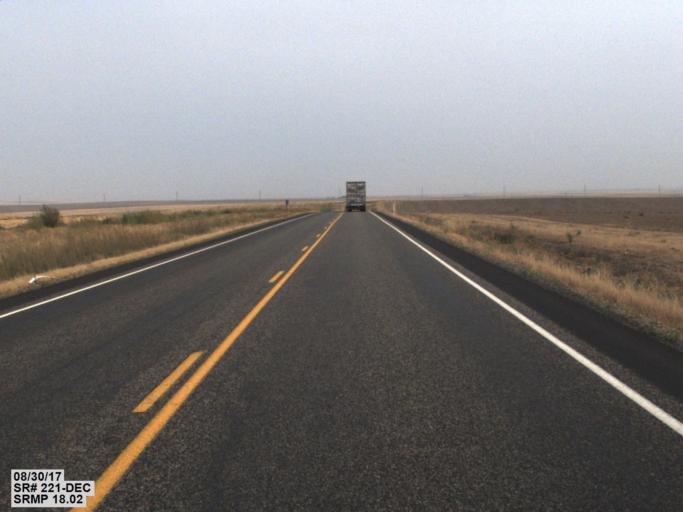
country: US
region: Washington
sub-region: Benton County
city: Benton City
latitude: 46.1867
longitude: -119.6164
